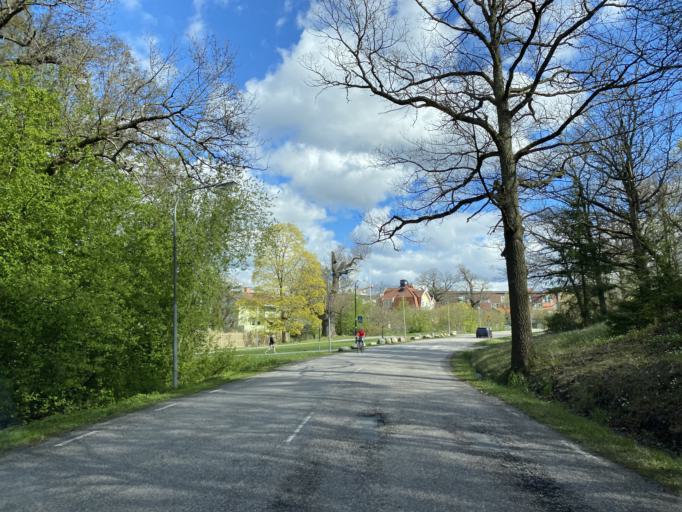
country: SE
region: Stockholm
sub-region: Stockholms Kommun
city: OEstermalm
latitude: 59.3558
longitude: 18.0838
